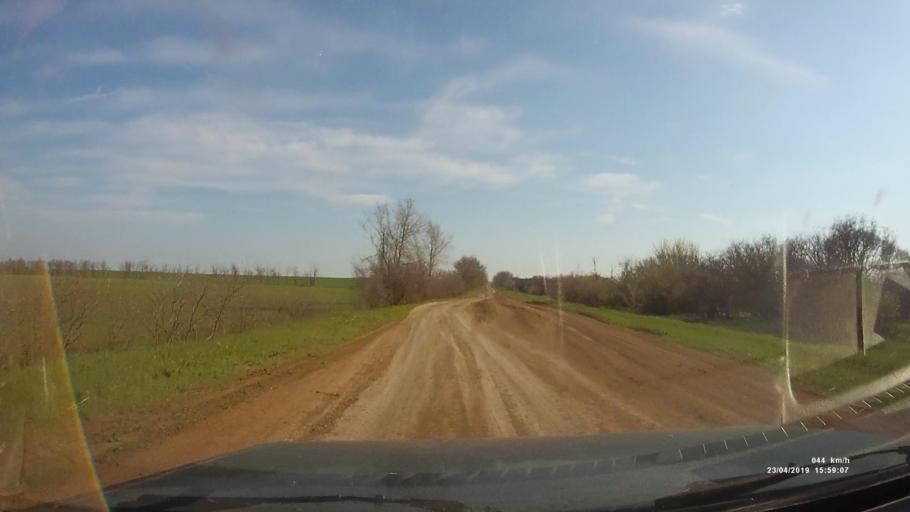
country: RU
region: Rostov
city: Remontnoye
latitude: 46.5200
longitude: 43.1095
